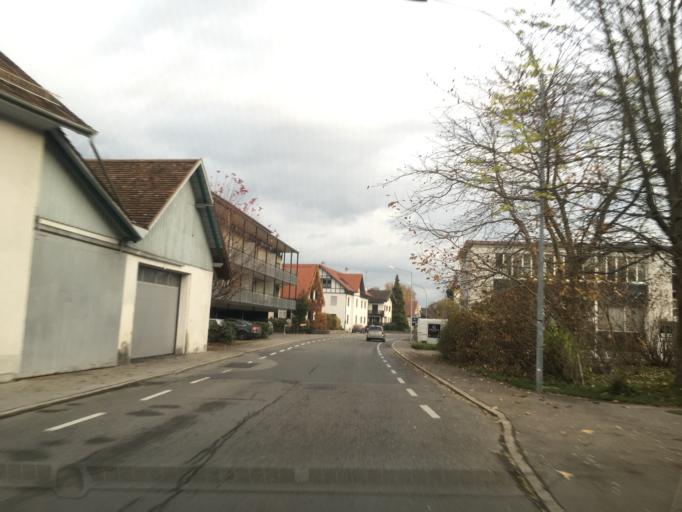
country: AT
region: Vorarlberg
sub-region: Politischer Bezirk Feldkirch
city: Gotzis
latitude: 47.3373
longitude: 9.6397
